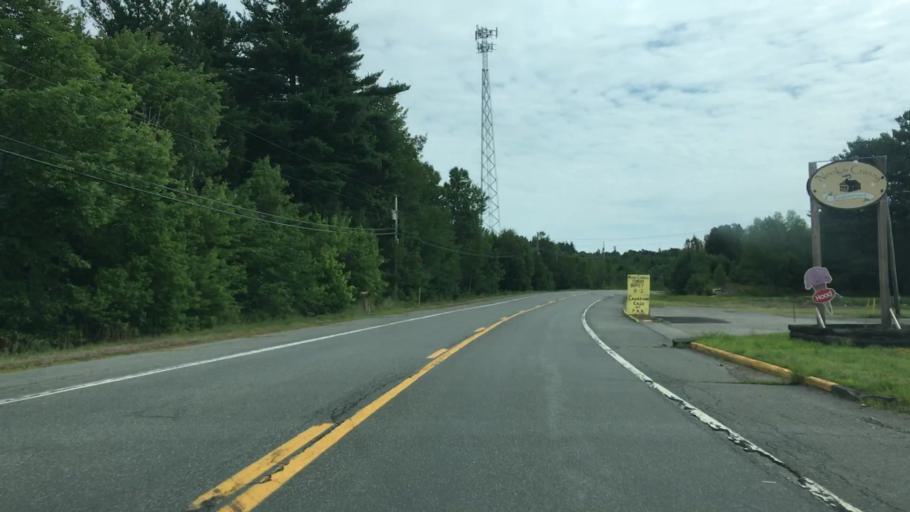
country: US
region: Maine
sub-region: Washington County
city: Calais
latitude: 45.1158
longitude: -67.4037
